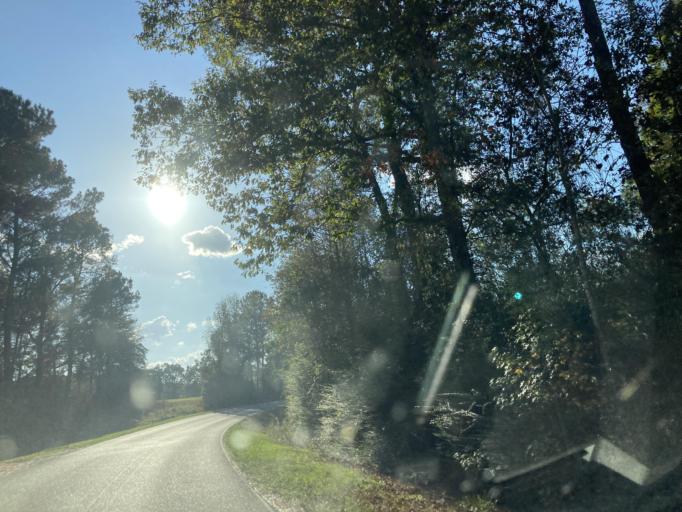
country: US
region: Mississippi
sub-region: Lamar County
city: Sumrall
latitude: 31.4083
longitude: -89.6477
